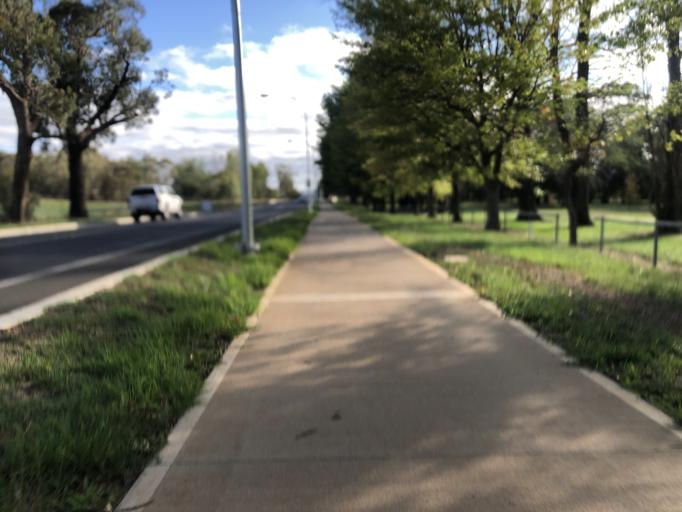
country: AU
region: New South Wales
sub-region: Orange Municipality
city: Orange
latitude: -33.3133
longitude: 149.0937
